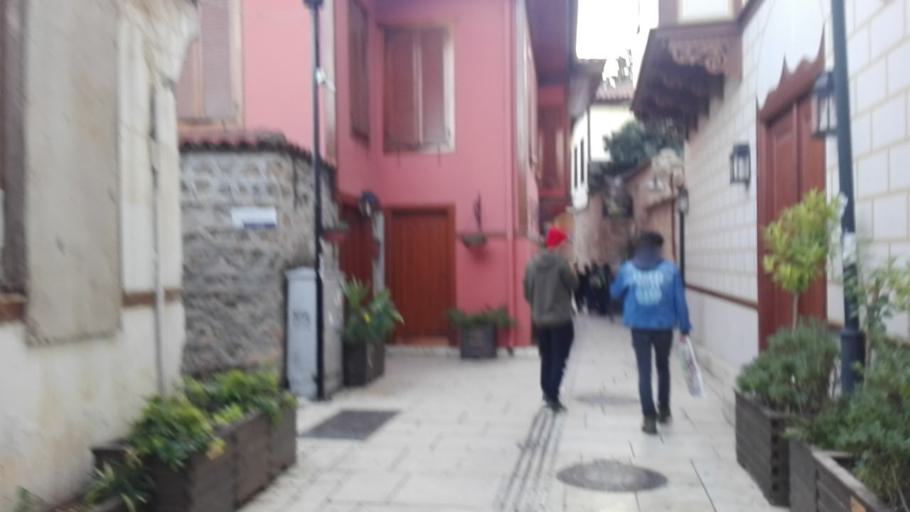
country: TR
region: Antalya
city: Antalya
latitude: 36.8842
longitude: 30.7073
